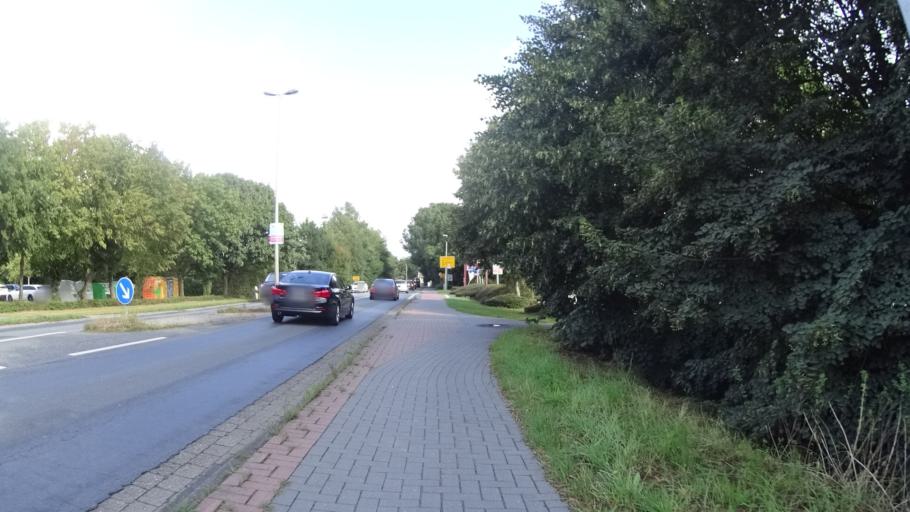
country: DE
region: Lower Saxony
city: Varel
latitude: 53.3902
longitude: 8.1514
